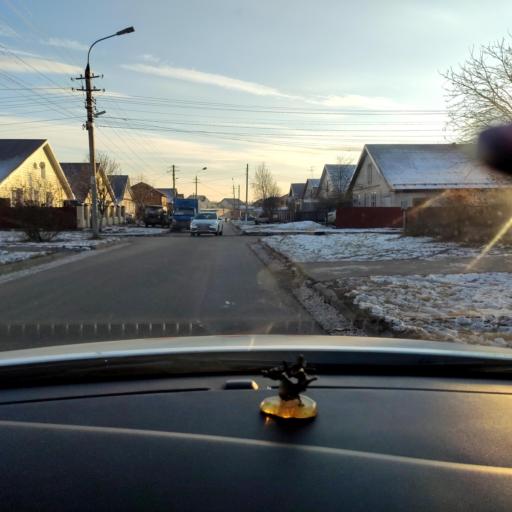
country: RU
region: Tatarstan
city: Stolbishchi
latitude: 55.6104
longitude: 49.1365
